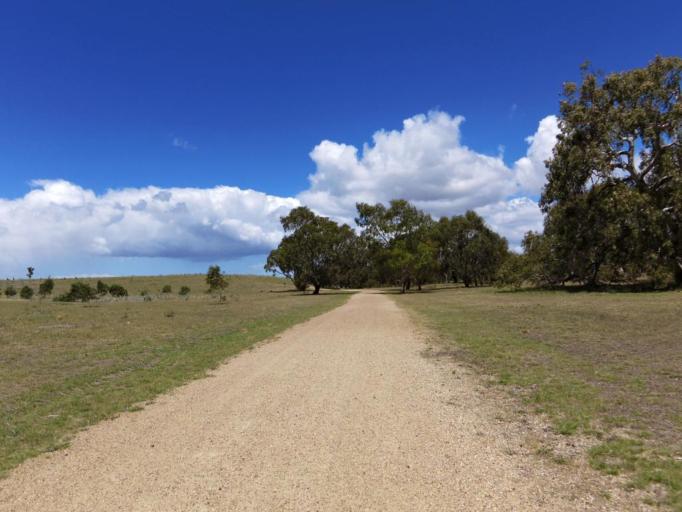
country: AU
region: Victoria
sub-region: Hume
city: Greenvale
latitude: -37.6512
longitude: 144.8472
